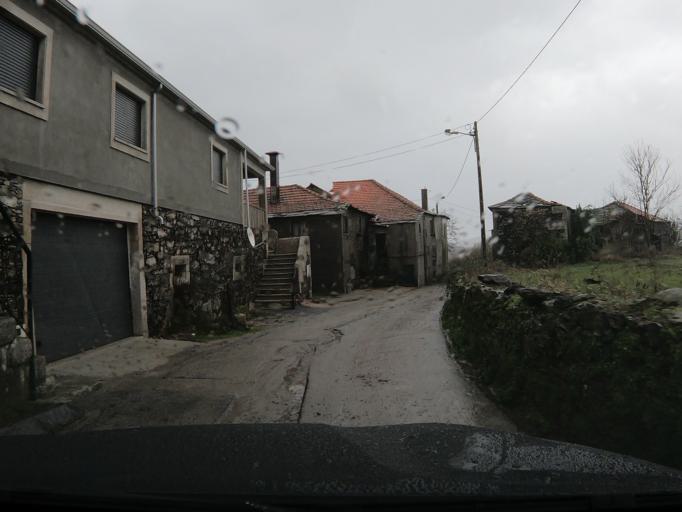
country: PT
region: Vila Real
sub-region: Santa Marta de Penaguiao
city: Santa Marta de Penaguiao
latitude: 41.2992
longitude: -7.8765
